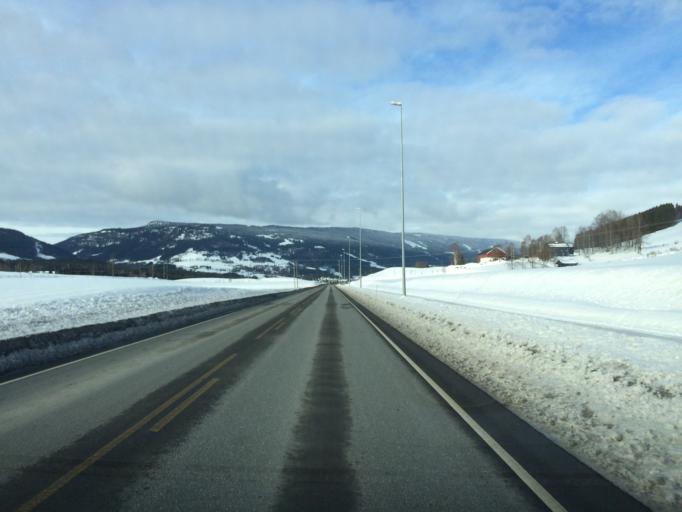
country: NO
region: Oppland
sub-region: Gausdal
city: Segalstad bru
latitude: 61.2204
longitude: 10.2489
